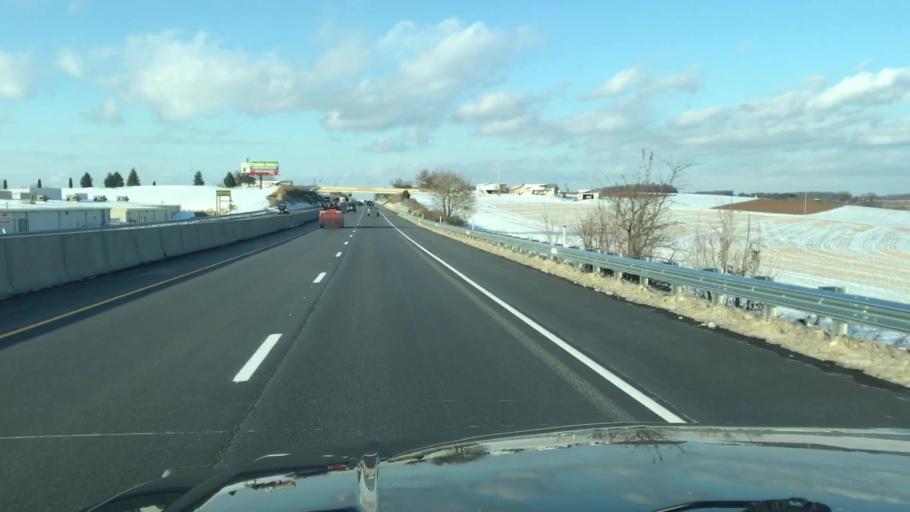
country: US
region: Pennsylvania
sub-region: York County
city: Shrewsbury
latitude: 39.8043
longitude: -76.6781
